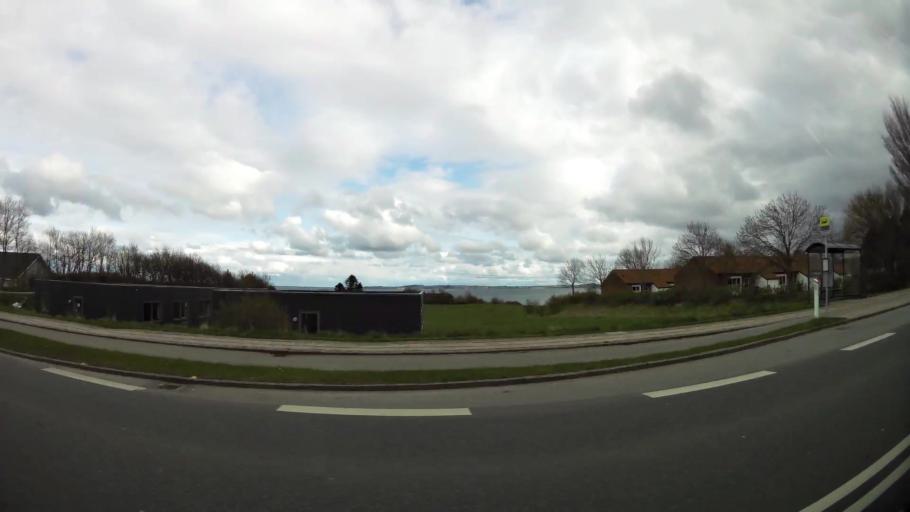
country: DK
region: North Denmark
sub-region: Thisted Kommune
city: Thisted
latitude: 56.9462
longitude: 8.6593
